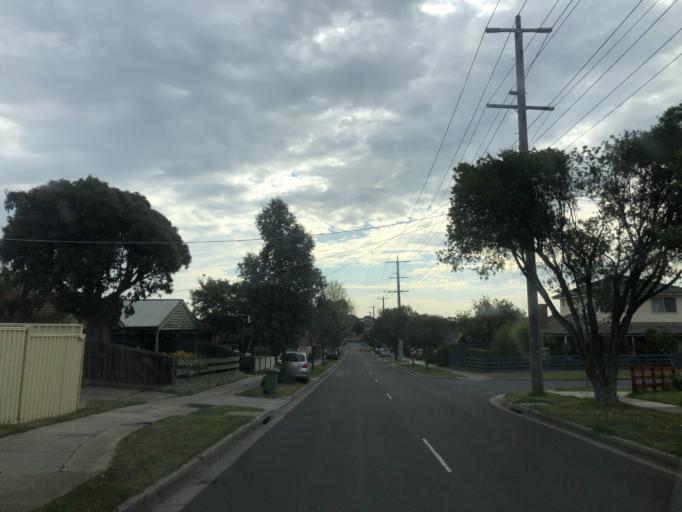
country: AU
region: Victoria
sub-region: Casey
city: Hampton Park
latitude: -38.0341
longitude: 145.2546
